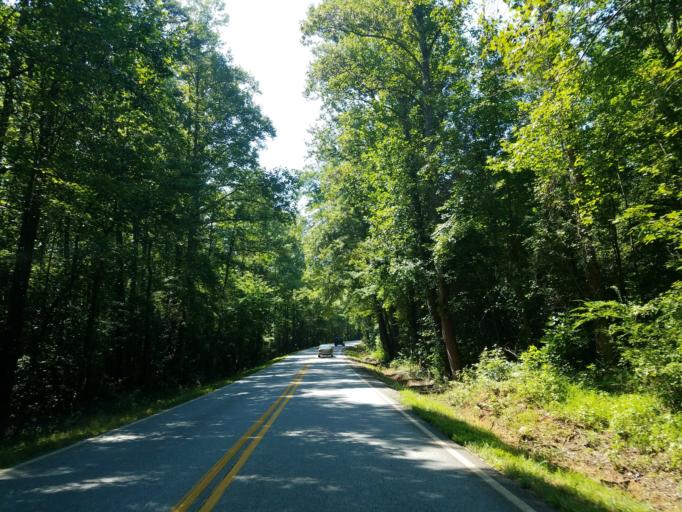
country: US
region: Georgia
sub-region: Lumpkin County
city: Dahlonega
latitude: 34.6258
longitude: -83.9458
